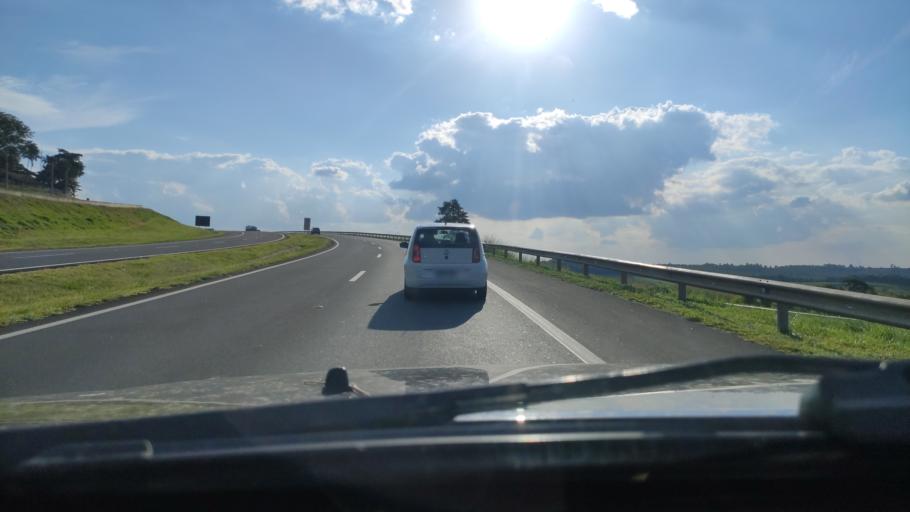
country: BR
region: Sao Paulo
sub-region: Itapira
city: Itapira
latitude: -22.4505
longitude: -46.8468
